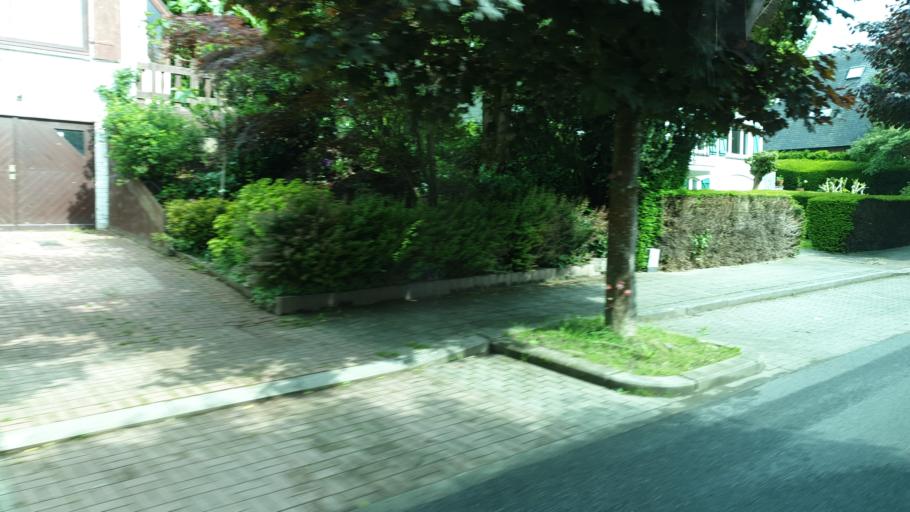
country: BE
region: Flanders
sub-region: Provincie Vlaams-Brabant
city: Wezembeek-Oppem
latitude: 50.8286
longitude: 4.4662
